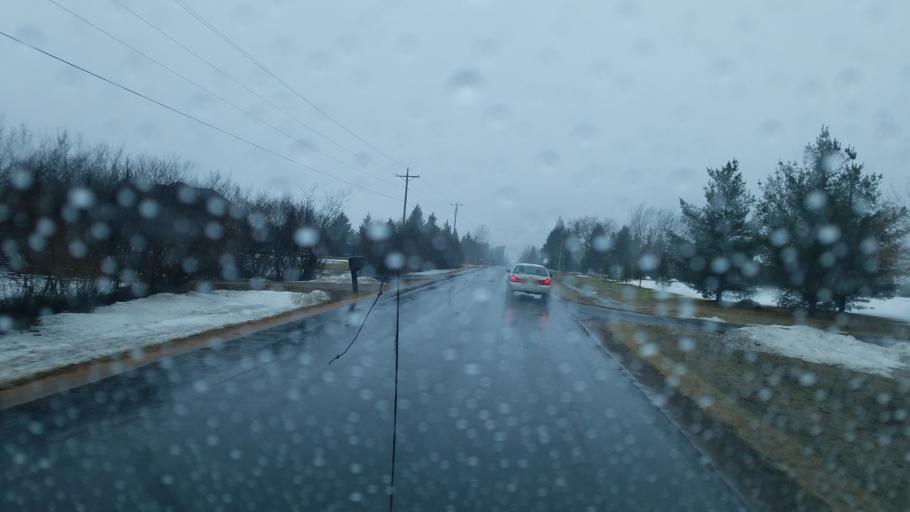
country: US
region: Wisconsin
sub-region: Wood County
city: Marshfield
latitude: 44.6772
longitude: -90.2079
